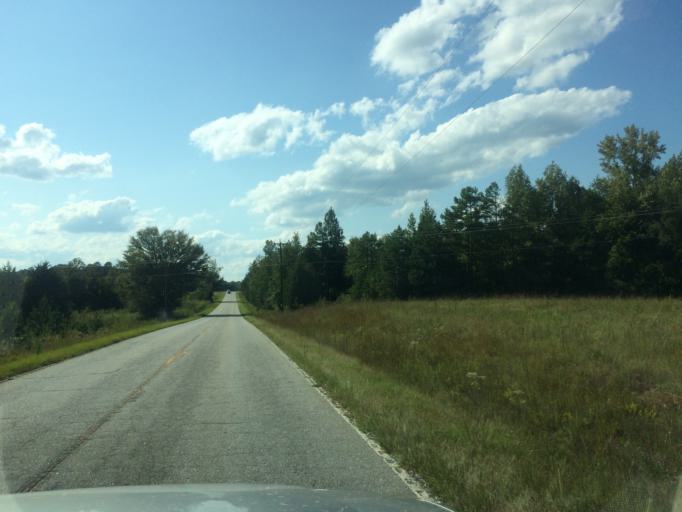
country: US
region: South Carolina
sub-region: Greenwood County
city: Ware Shoals
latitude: 34.4639
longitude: -82.1730
